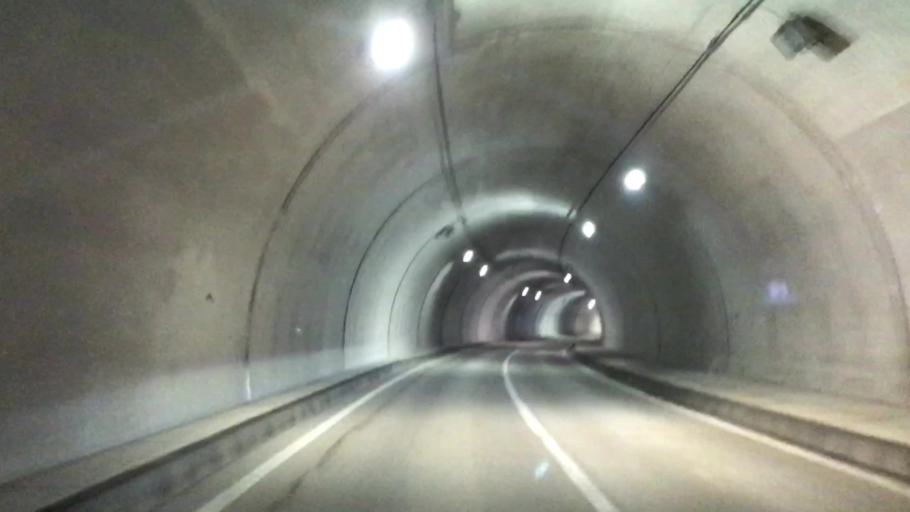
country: JP
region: Hokkaido
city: Iwanai
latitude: 43.3306
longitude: 140.3751
